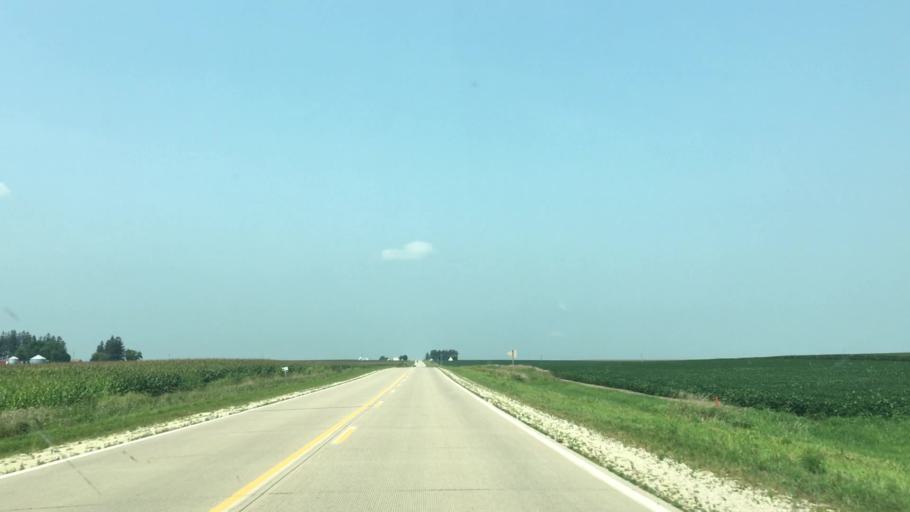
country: US
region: Iowa
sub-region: Fayette County
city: Oelwein
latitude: 42.6960
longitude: -91.8050
